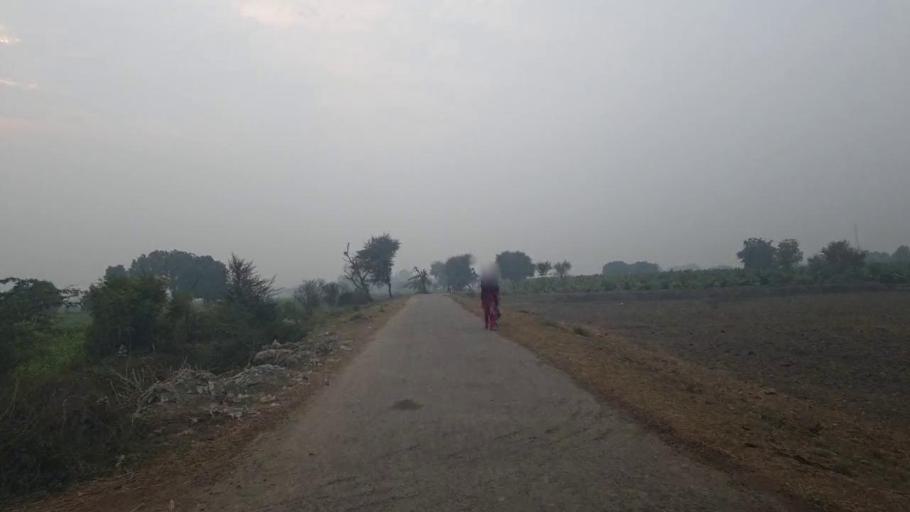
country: PK
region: Sindh
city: Tando Adam
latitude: 25.7373
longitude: 68.6693
